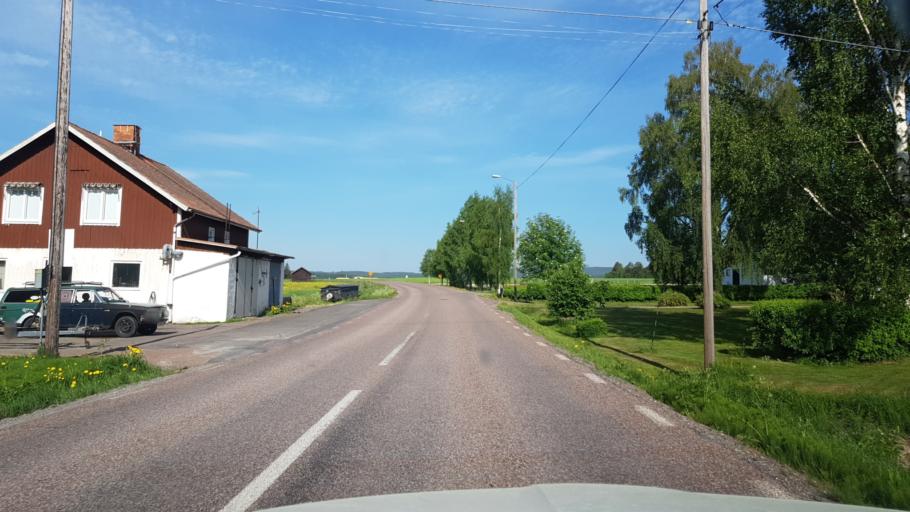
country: SE
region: Dalarna
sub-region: Saters Kommun
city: Saeter
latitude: 60.4159
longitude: 15.7639
